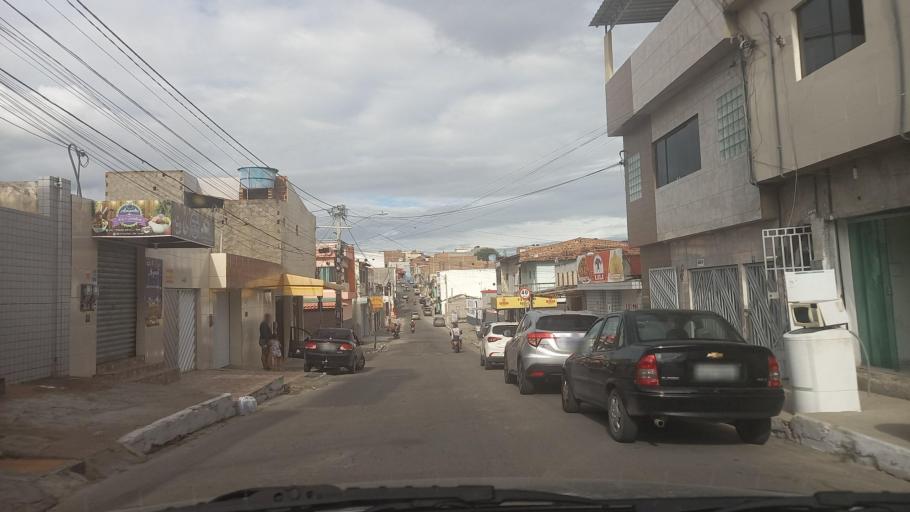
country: BR
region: Pernambuco
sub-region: Caruaru
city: Caruaru
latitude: -8.2853
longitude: -35.9891
